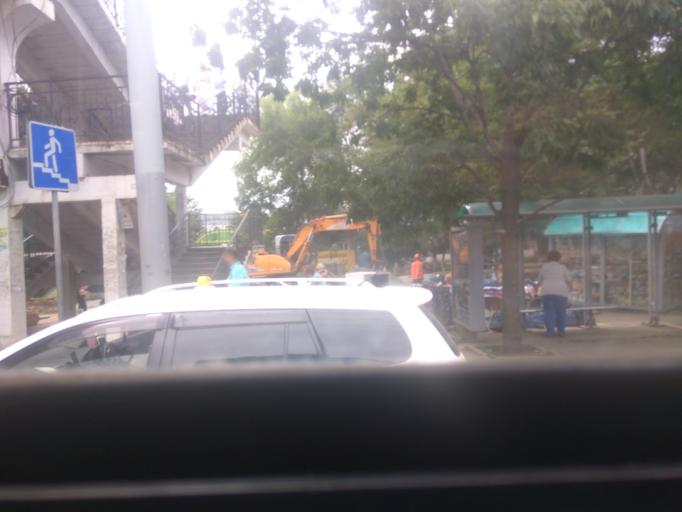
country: RU
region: Primorskiy
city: Vladivostok
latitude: 43.1649
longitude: 131.9136
